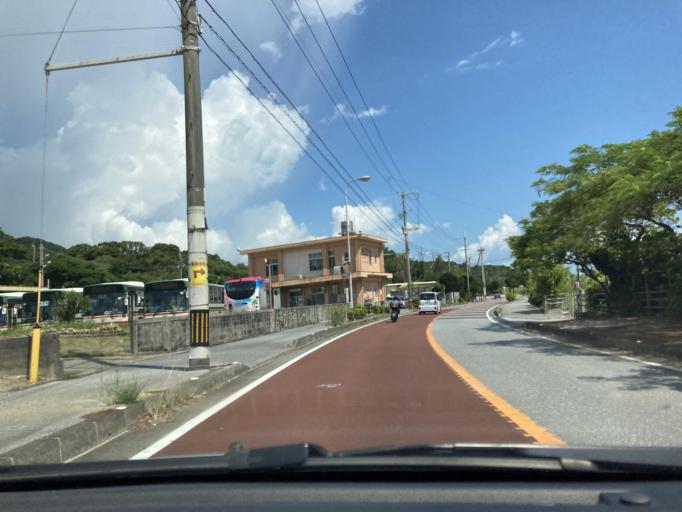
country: JP
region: Okinawa
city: Tomigusuku
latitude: 26.1767
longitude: 127.7674
